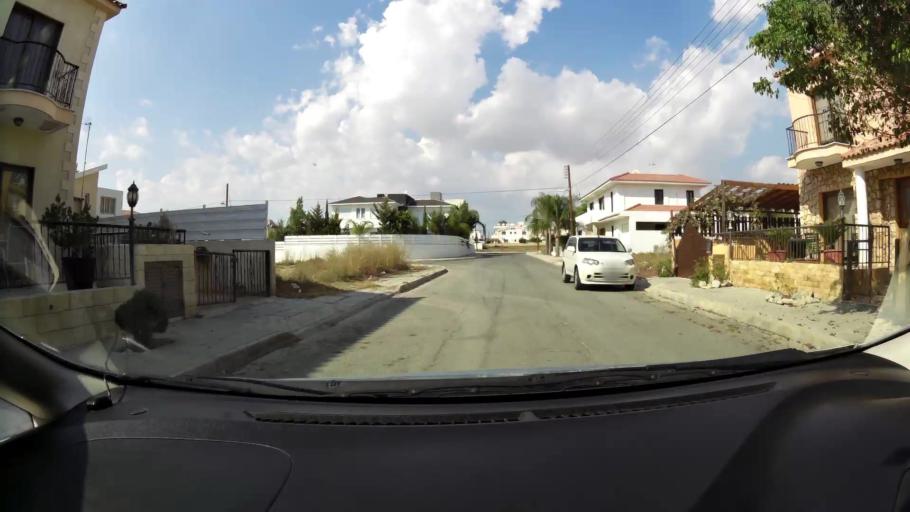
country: CY
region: Larnaka
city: Dhromolaxia
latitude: 34.9044
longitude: 33.5846
